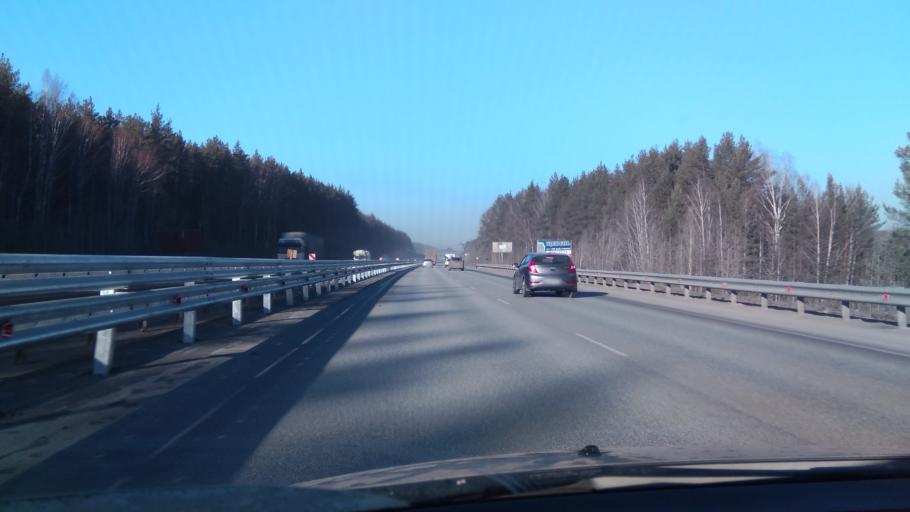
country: RU
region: Sverdlovsk
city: Severka
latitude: 56.8320
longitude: 60.3479
